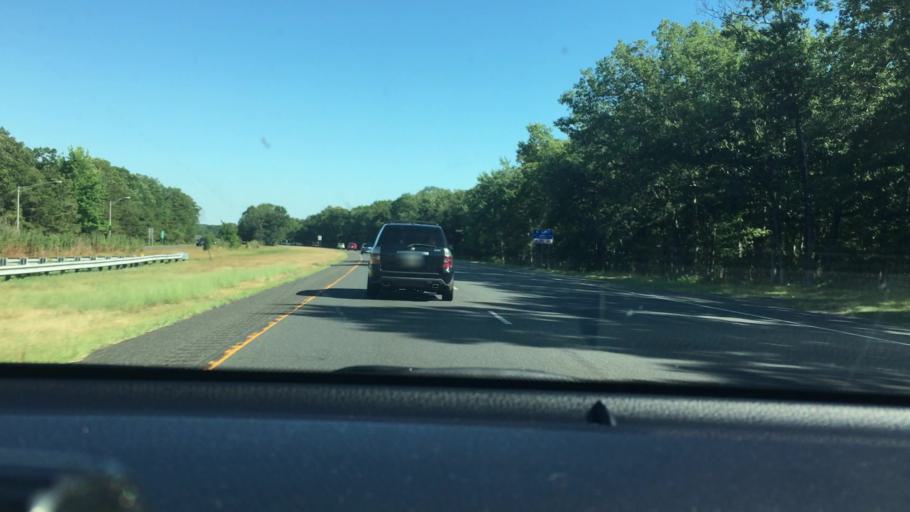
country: US
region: New Jersey
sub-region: Gloucester County
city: Newfield
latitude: 39.5779
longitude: -75.0711
